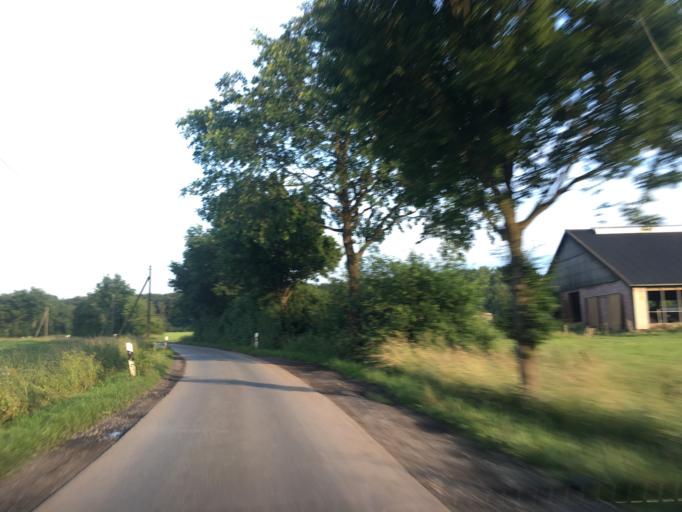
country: DE
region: North Rhine-Westphalia
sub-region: Regierungsbezirk Munster
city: Senden
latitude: 51.9058
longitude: 7.5453
